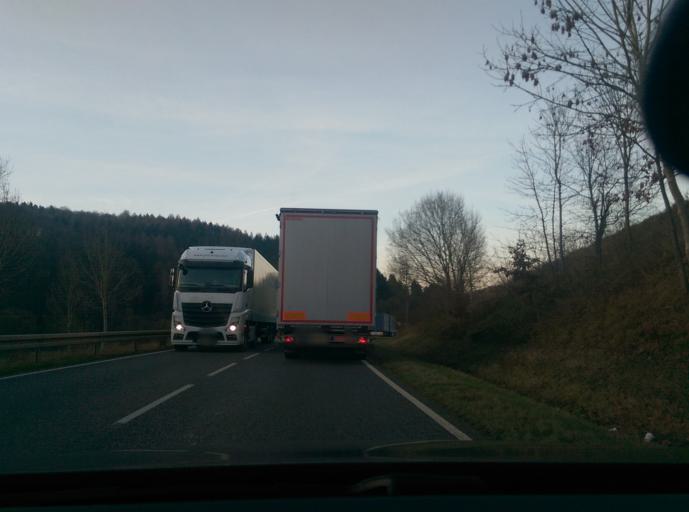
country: DE
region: Hesse
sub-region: Regierungsbezirk Kassel
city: Sontra
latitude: 51.0744
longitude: 9.9905
